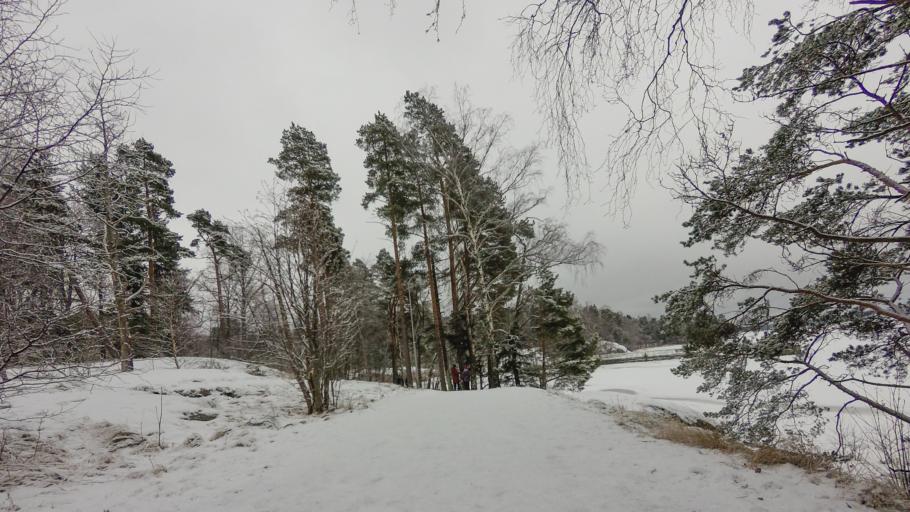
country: FI
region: Uusimaa
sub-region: Helsinki
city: Teekkarikylae
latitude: 60.1812
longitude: 24.8804
